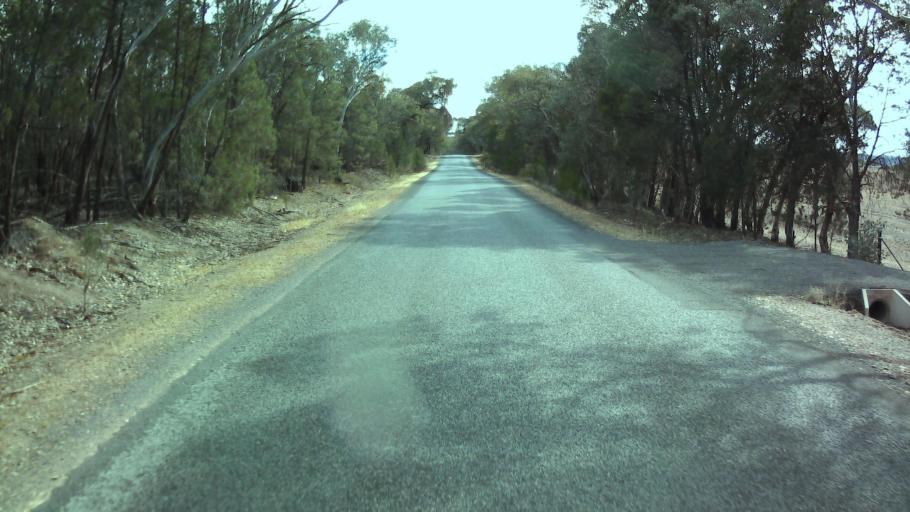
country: AU
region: New South Wales
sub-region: Weddin
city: Grenfell
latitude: -33.8928
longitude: 148.1900
